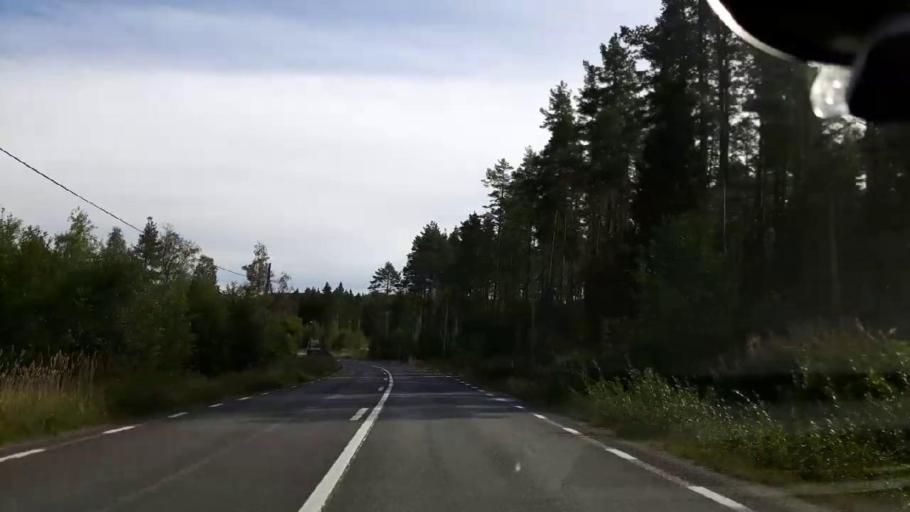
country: SE
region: Jaemtland
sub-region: Braecke Kommun
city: Braecke
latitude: 63.1620
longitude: 15.5738
